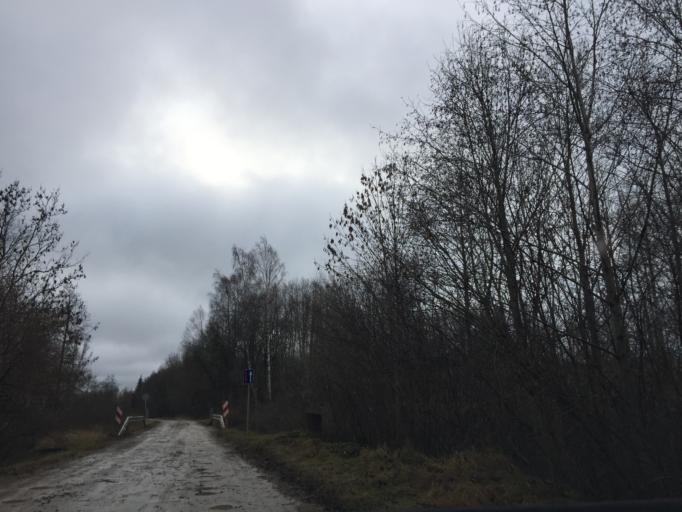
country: LV
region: Broceni
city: Broceni
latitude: 56.6633
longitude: 22.5522
